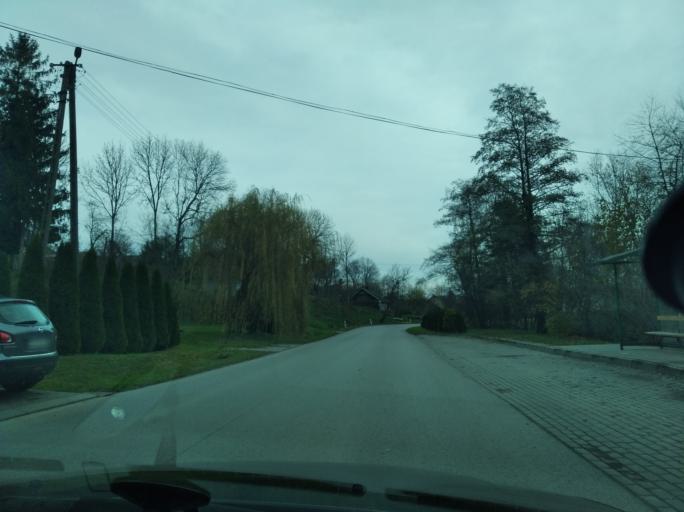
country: PL
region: Subcarpathian Voivodeship
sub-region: Powiat przeworski
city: Gac
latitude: 50.0286
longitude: 22.3673
